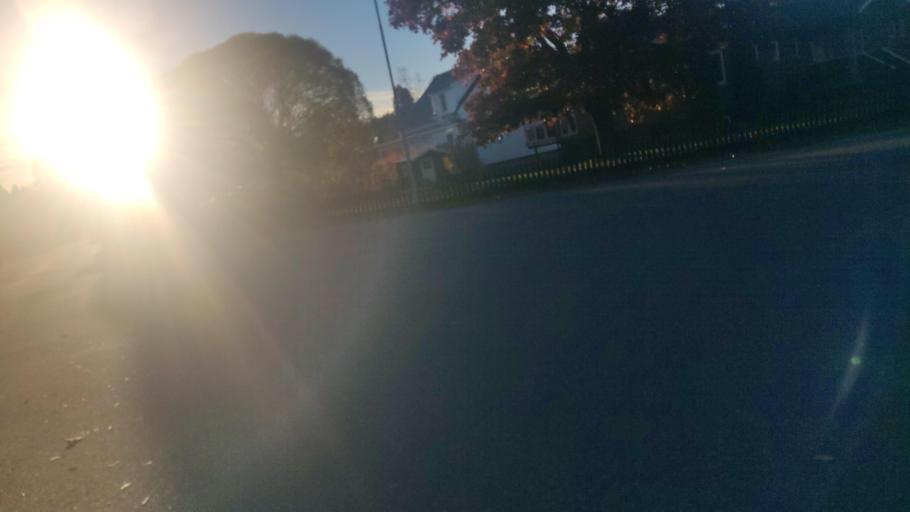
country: SE
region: Vaesternorrland
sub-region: Sundsvalls Kommun
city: Njurundabommen
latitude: 62.2702
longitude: 17.3935
